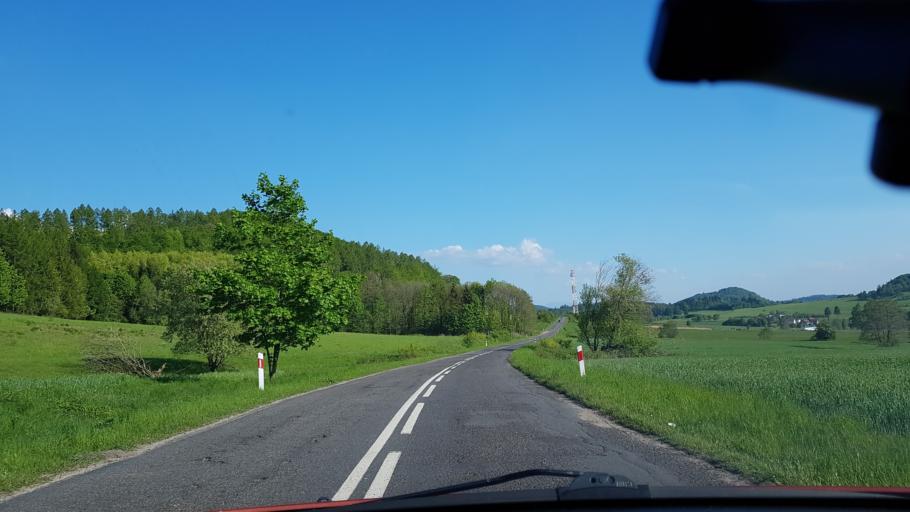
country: PL
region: Lower Silesian Voivodeship
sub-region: Powiat klodzki
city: Bozkow
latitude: 50.5862
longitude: 16.5826
